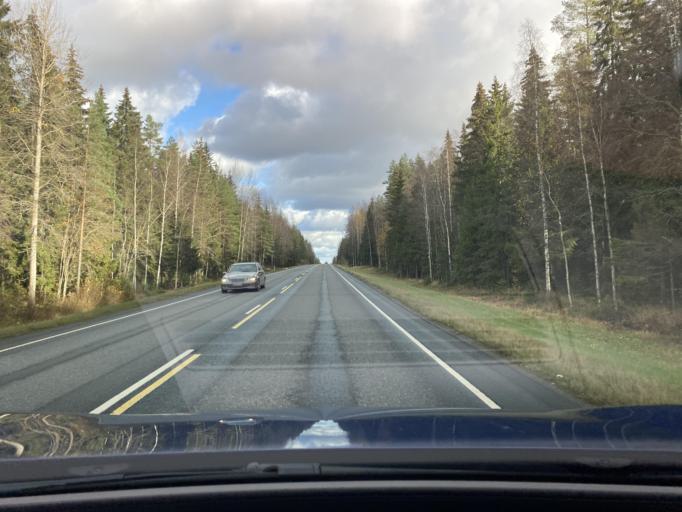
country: FI
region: Haeme
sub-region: Forssa
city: Humppila
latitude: 60.9374
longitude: 23.2674
